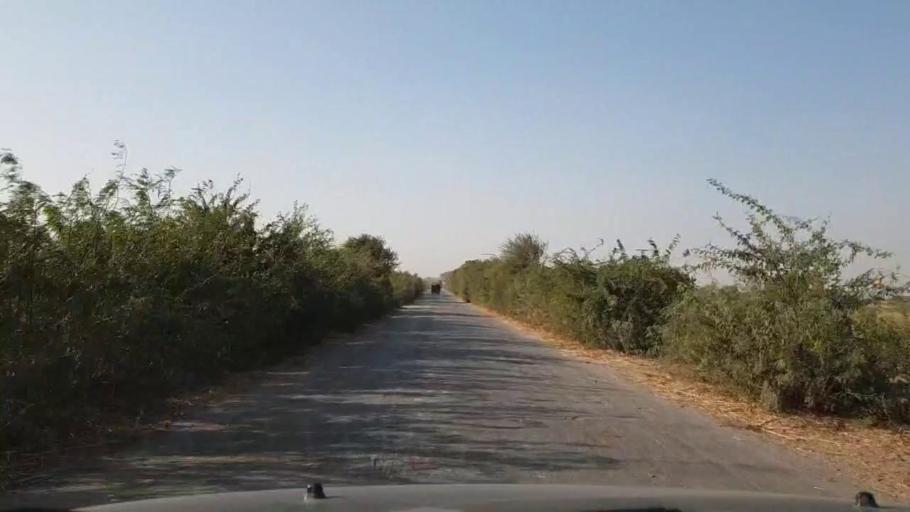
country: PK
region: Sindh
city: Tando Ghulam Ali
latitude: 25.1519
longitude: 68.8584
